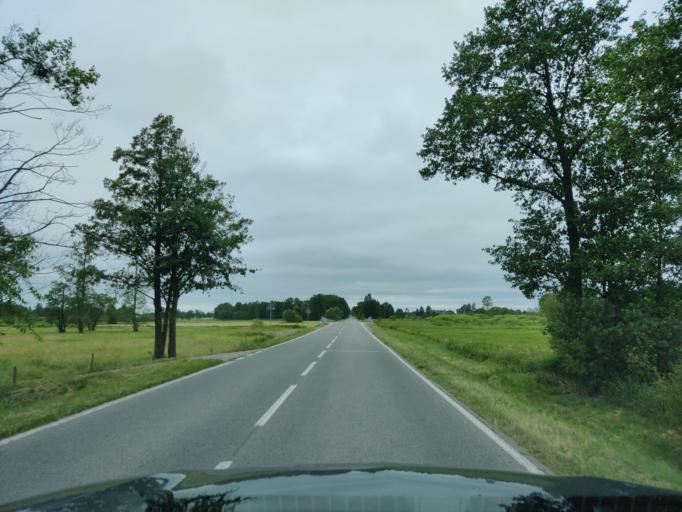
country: PL
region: Masovian Voivodeship
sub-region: Powiat ostrolecki
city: Czarnia
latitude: 53.3252
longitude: 21.1644
